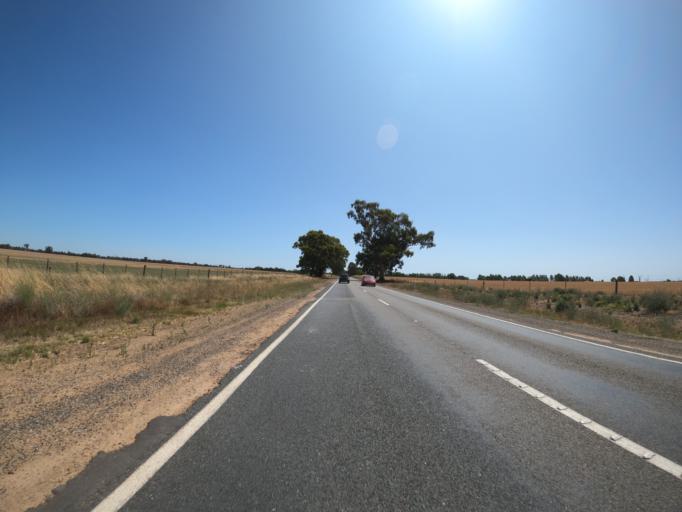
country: AU
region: Victoria
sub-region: Moira
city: Yarrawonga
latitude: -36.0249
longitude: 146.1030
